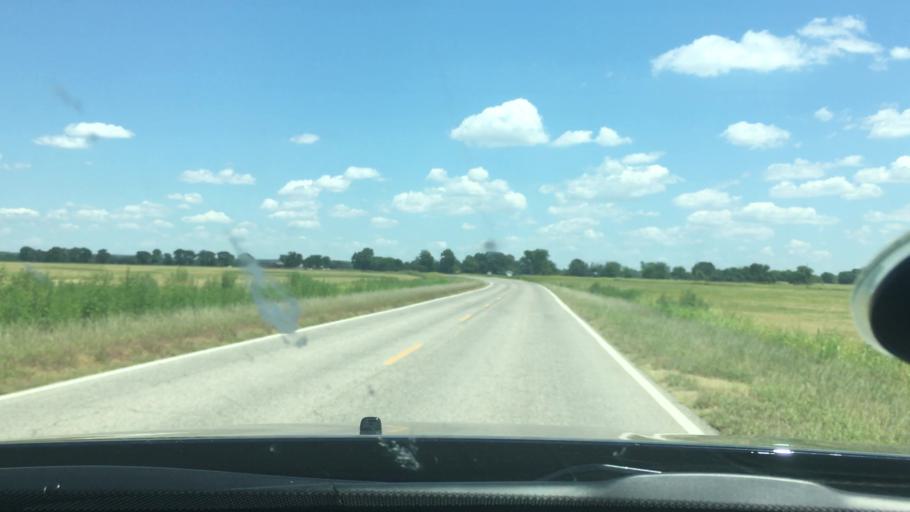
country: US
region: Oklahoma
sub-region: Carter County
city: Dickson
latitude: 34.2488
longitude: -96.9705
